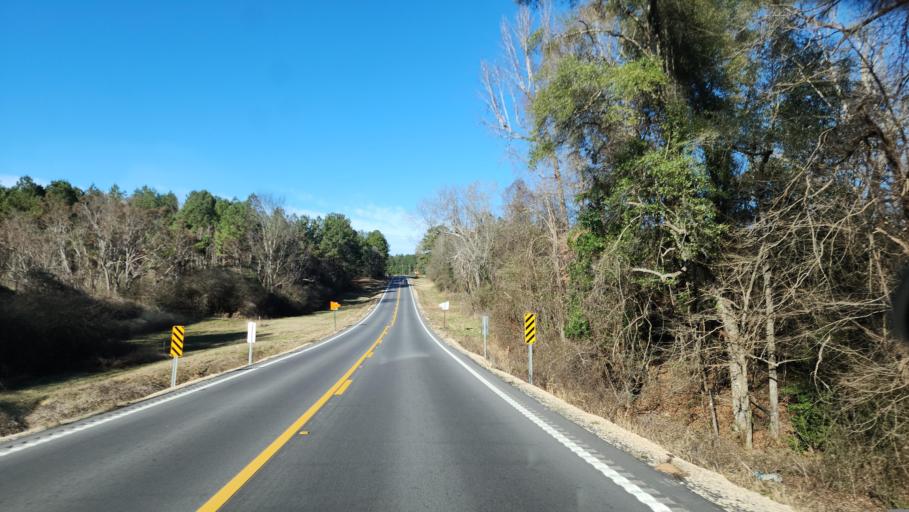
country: US
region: Mississippi
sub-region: Wayne County
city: Waynesboro
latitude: 31.7202
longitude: -88.6446
